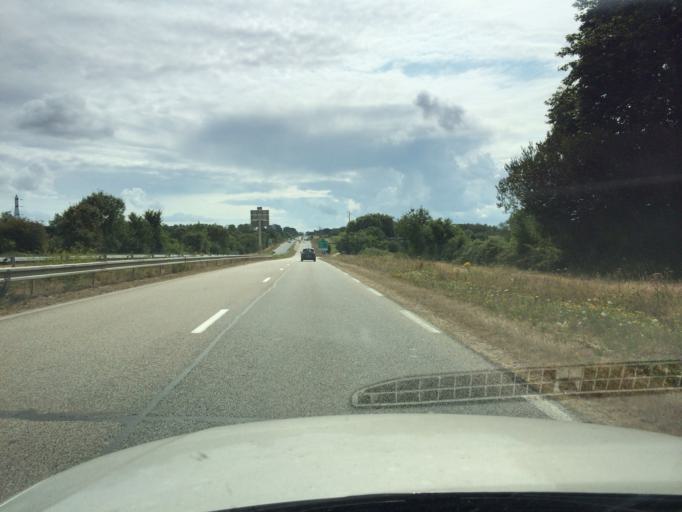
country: FR
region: Lower Normandy
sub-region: Departement de la Manche
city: Valognes
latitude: 49.4984
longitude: -1.4413
